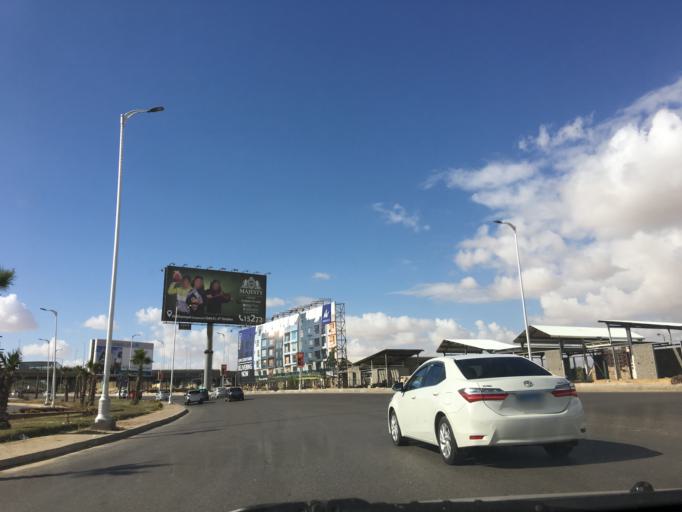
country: EG
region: Al Jizah
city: Awsim
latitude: 30.0095
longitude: 30.9848
